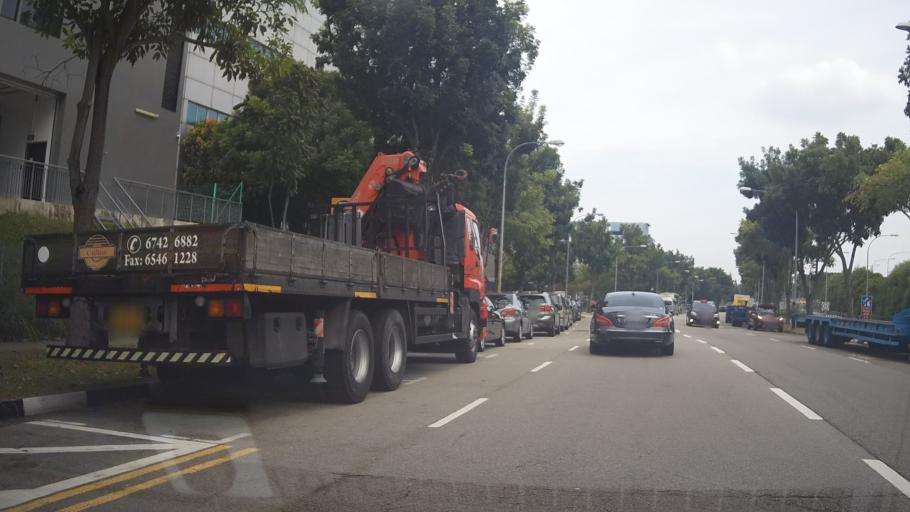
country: SG
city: Singapore
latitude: 1.3484
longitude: 103.9667
